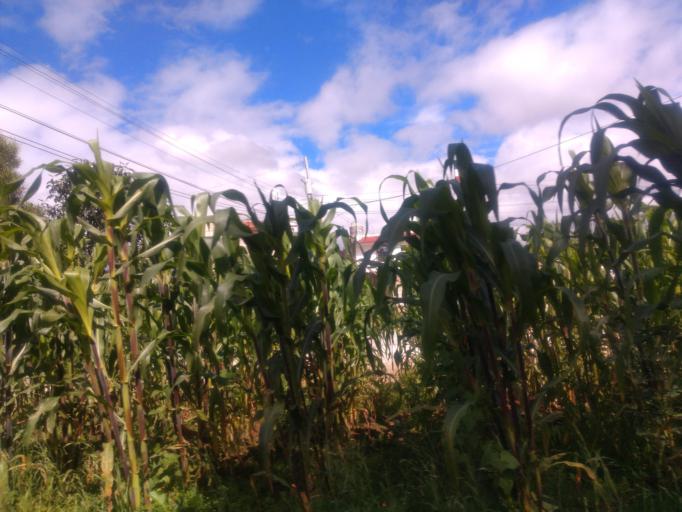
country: GT
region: Quetzaltenango
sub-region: Municipio de La Esperanza
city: La Esperanza
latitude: 14.8567
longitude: -91.5673
